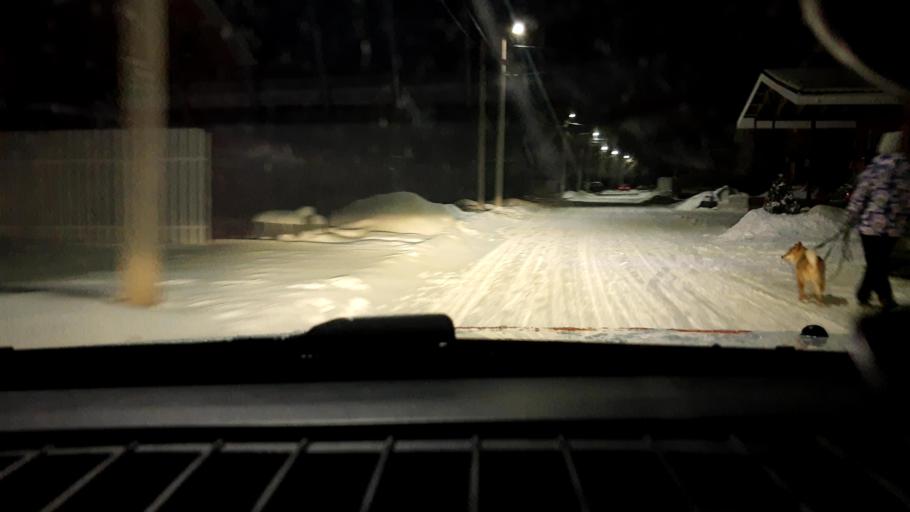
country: RU
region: Nizjnij Novgorod
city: Afonino
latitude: 56.1960
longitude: 44.0684
